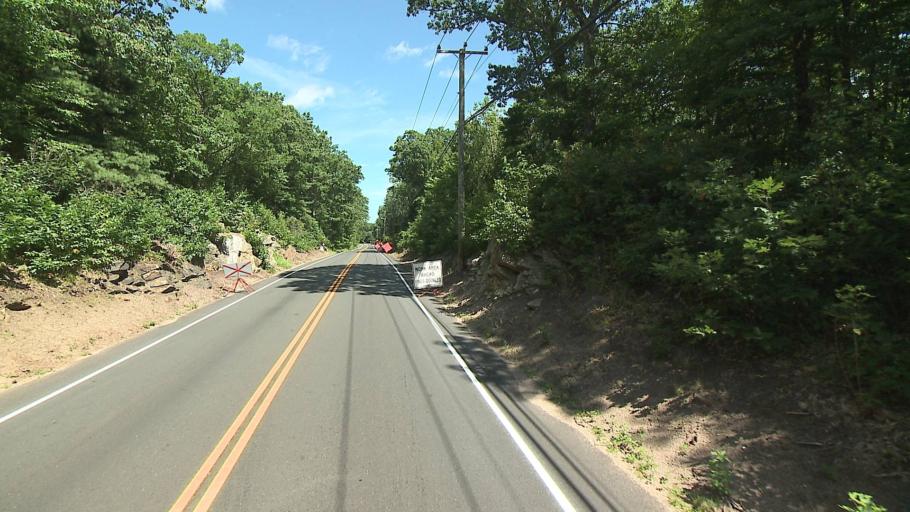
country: US
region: Connecticut
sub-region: Litchfield County
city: New Hartford Center
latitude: 41.9502
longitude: -72.9161
